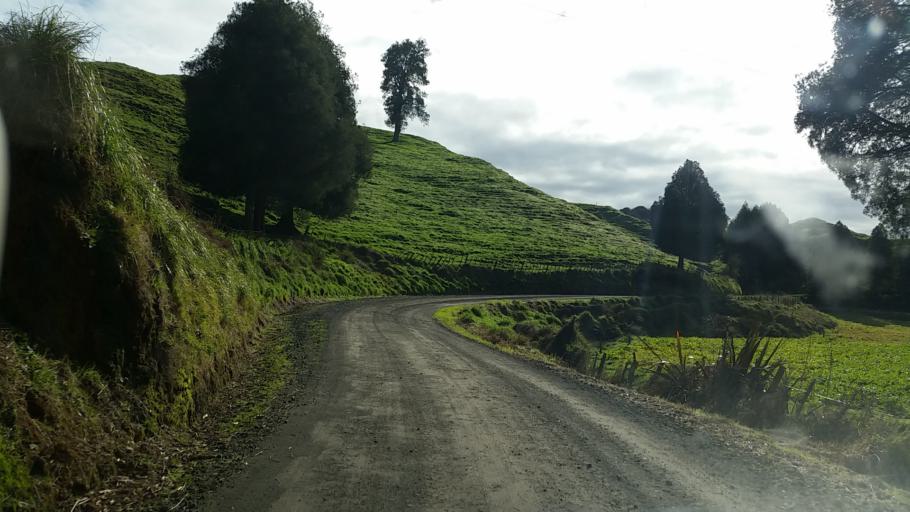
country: NZ
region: Taranaki
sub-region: South Taranaki District
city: Eltham
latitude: -39.2565
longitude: 174.5183
